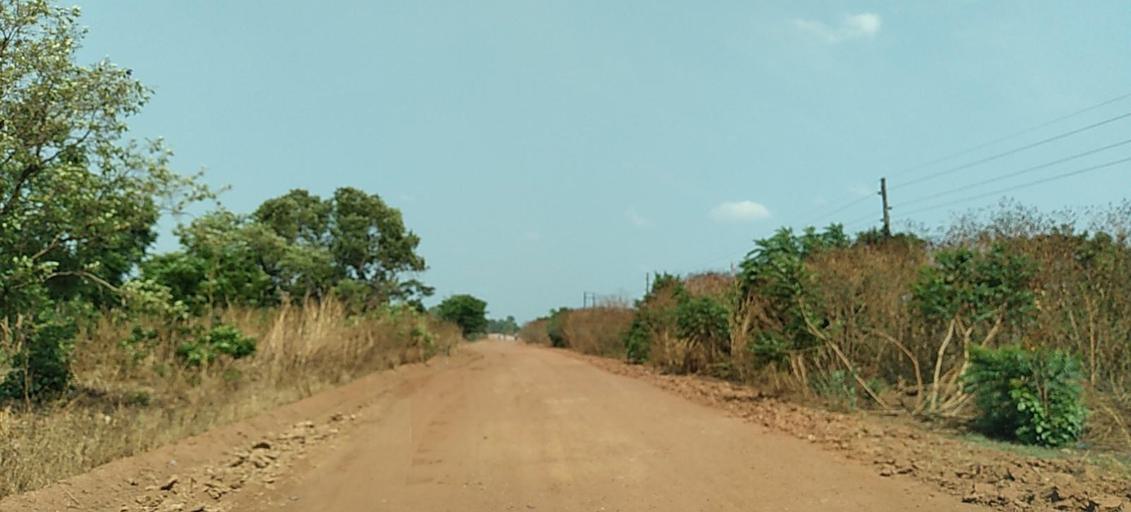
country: ZM
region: Copperbelt
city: Luanshya
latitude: -13.0942
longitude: 28.3151
